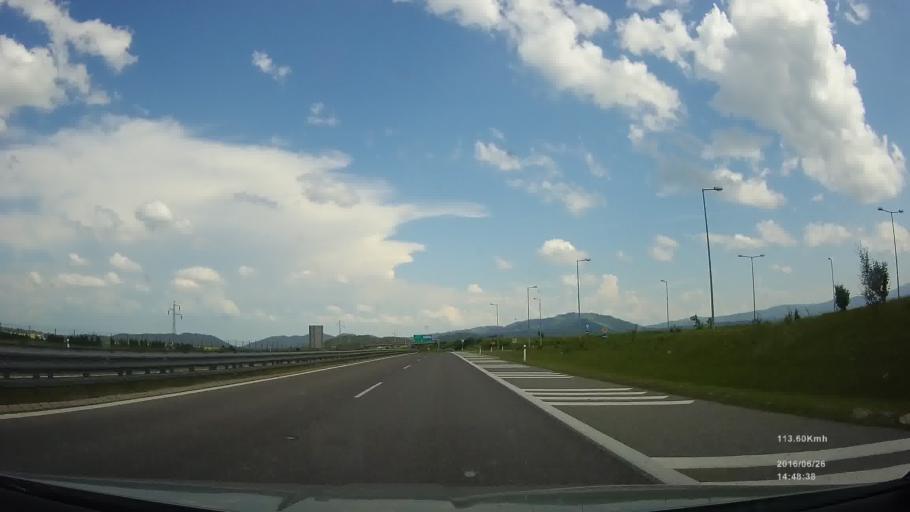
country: SK
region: Presovsky
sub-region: Okres Poprad
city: Strba
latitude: 49.0653
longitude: 20.0669
